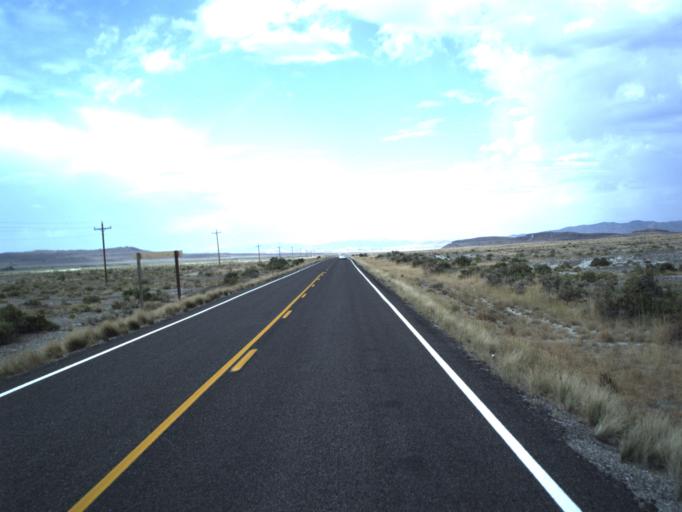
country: US
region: Utah
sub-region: Tooele County
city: Wendover
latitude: 41.4275
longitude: -113.8323
